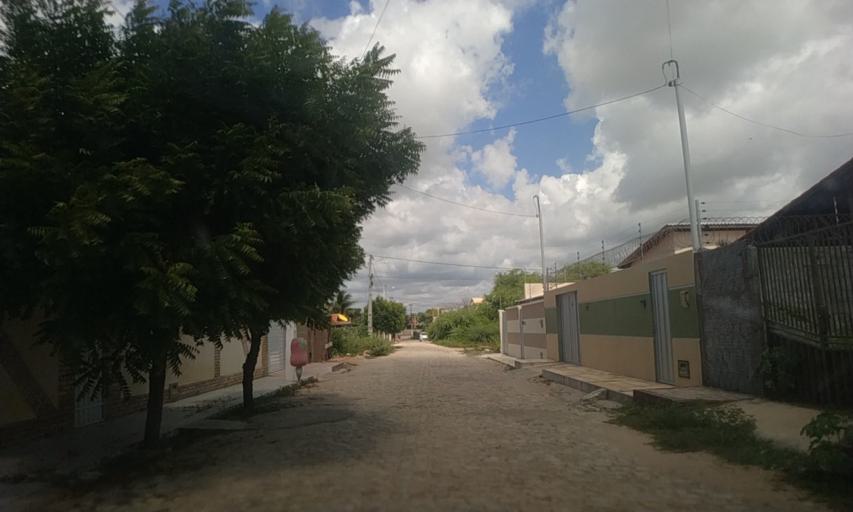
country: BR
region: Rio Grande do Norte
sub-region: Areia Branca
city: Areia Branca
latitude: -4.9289
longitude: -37.1104
